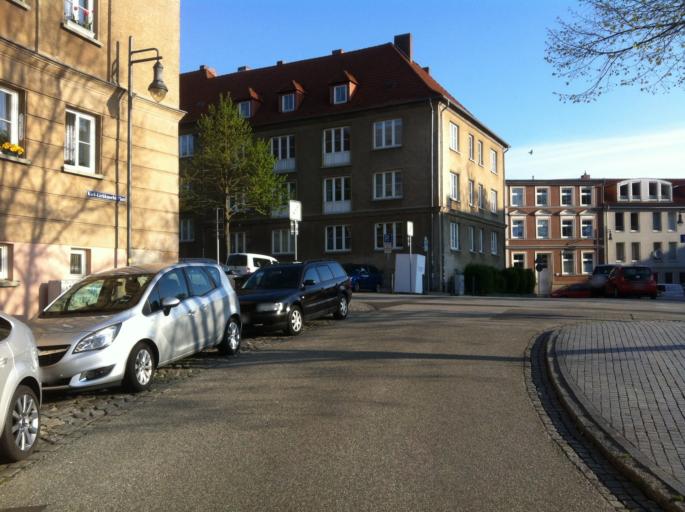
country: DE
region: Mecklenburg-Vorpommern
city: Feldstadt
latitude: 53.6232
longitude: 11.4046
